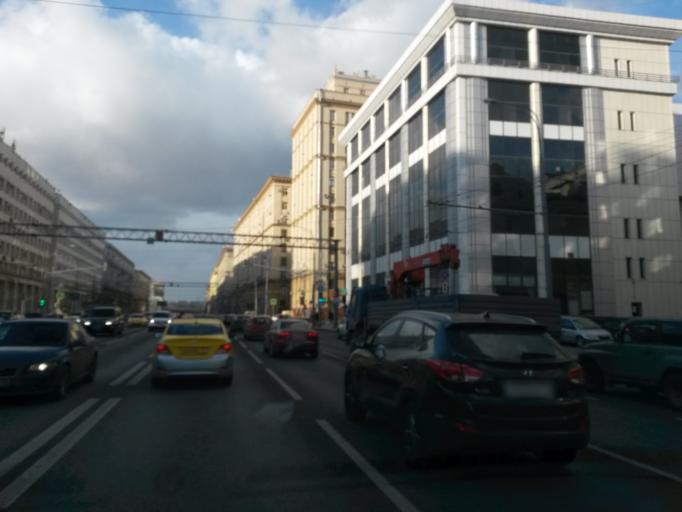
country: RU
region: Moscow
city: Mar'ina Roshcha
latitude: 55.7855
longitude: 37.6350
